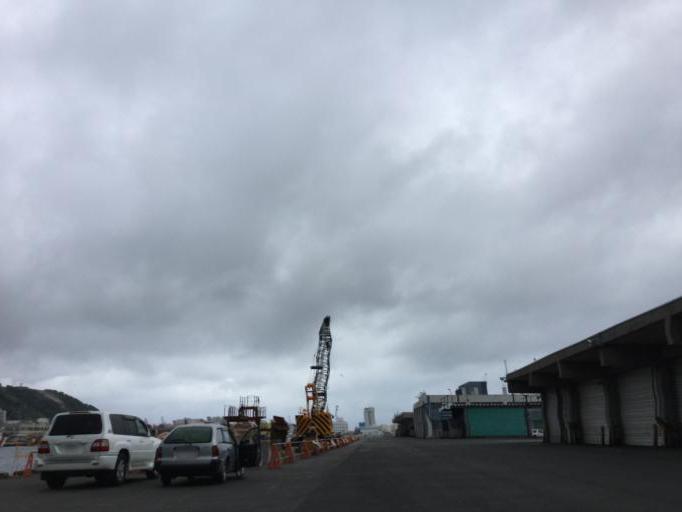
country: JP
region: Hokkaido
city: Wakkanai
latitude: 45.4068
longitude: 141.6792
